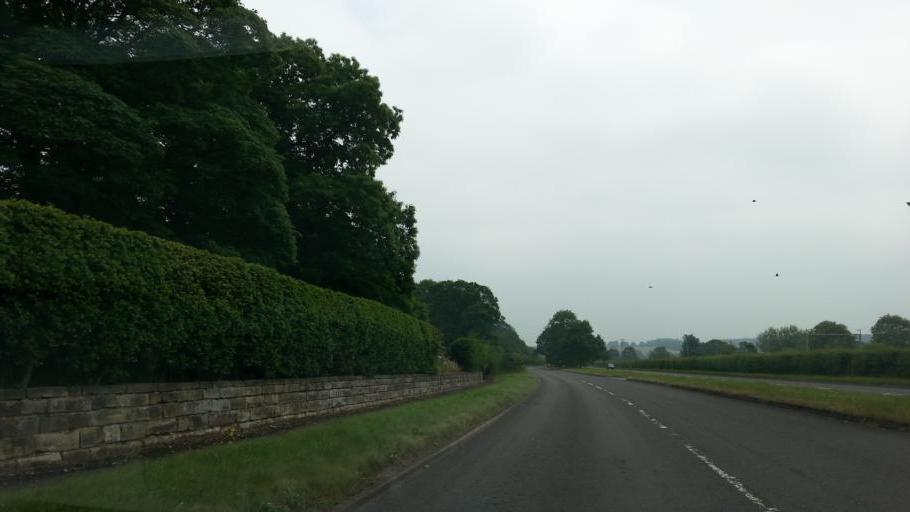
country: GB
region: England
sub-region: Staffordshire
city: Stafford
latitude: 52.8583
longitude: -2.0753
